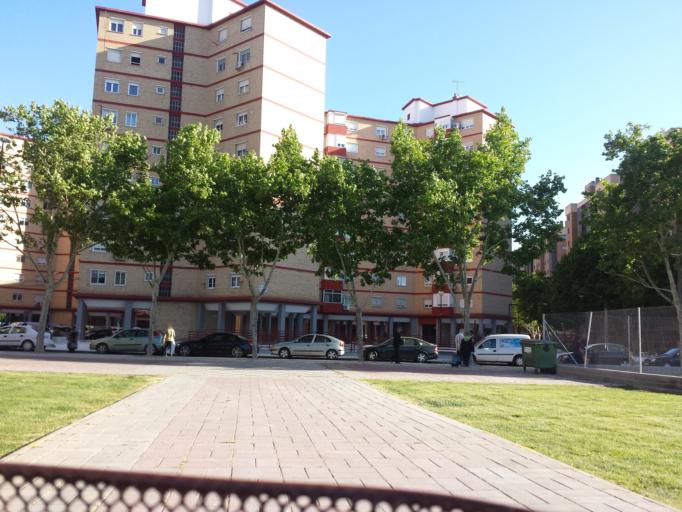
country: ES
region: Aragon
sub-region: Provincia de Zaragoza
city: Zaragoza
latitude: 41.6556
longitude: -0.8573
